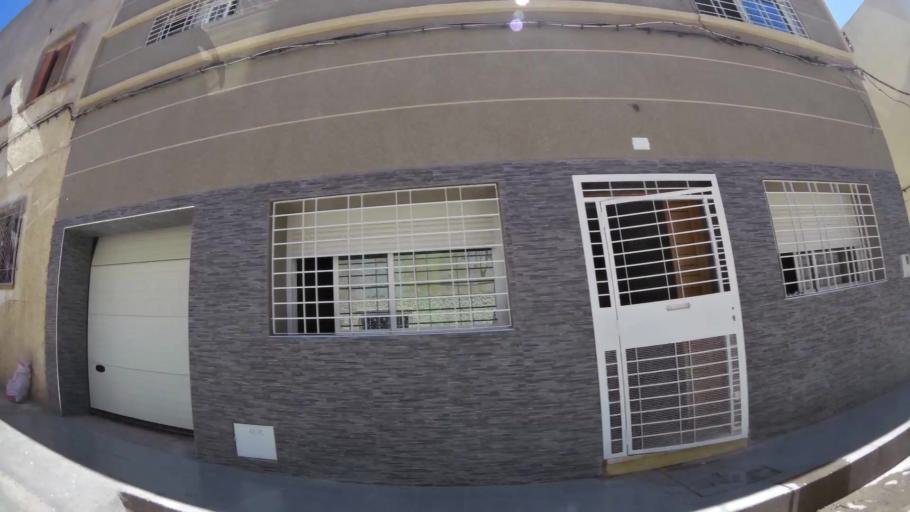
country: MA
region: Oriental
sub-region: Oujda-Angad
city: Oujda
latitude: 34.6685
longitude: -1.9242
